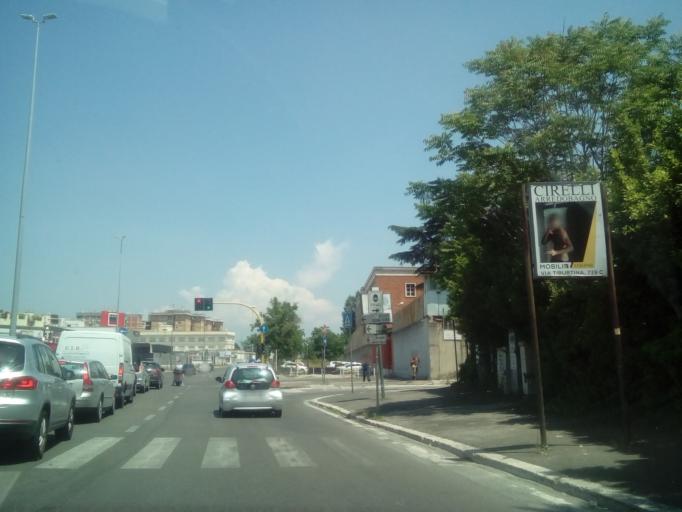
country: IT
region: Latium
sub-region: Citta metropolitana di Roma Capitale
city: Rome
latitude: 41.9126
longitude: 12.5551
